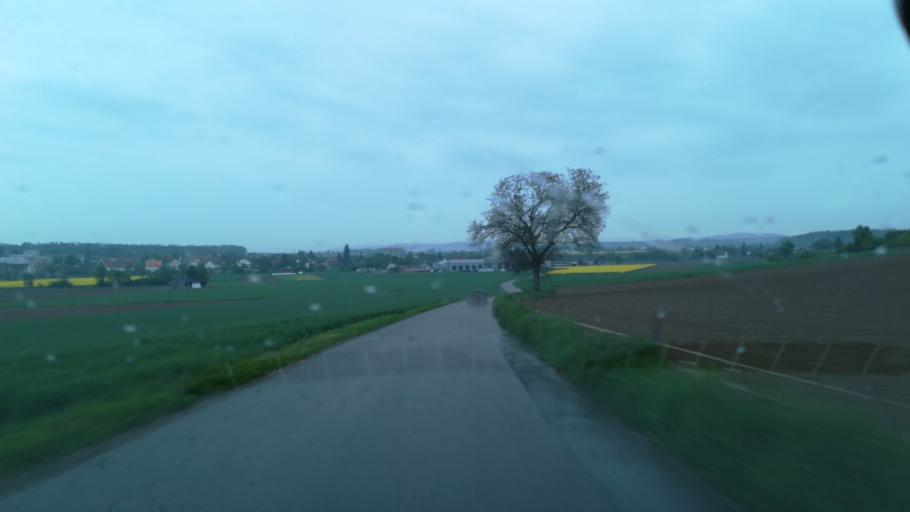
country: CH
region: Zurich
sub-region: Bezirk Buelach
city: End-Hoeri
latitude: 47.5160
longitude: 8.5008
